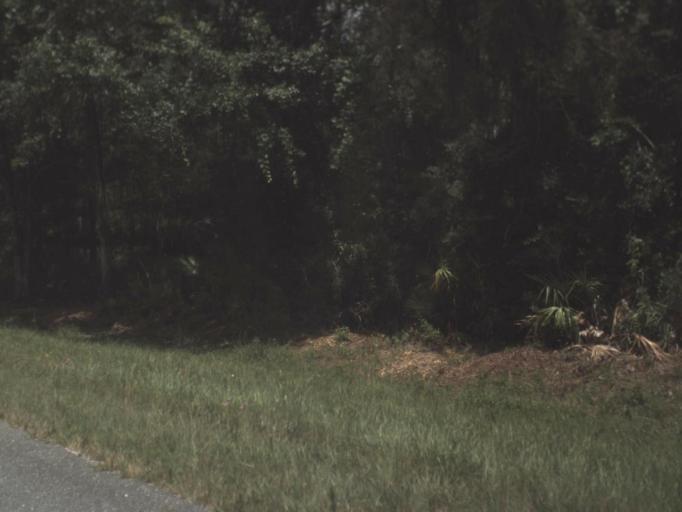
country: US
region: Florida
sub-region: Taylor County
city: Perry
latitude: 30.1411
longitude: -83.9173
